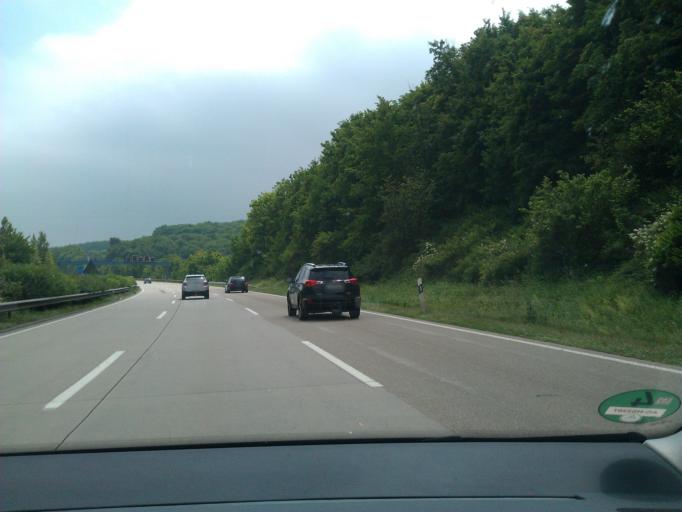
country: DE
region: Rheinland-Pfalz
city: Waldorf
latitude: 50.4827
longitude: 7.2187
